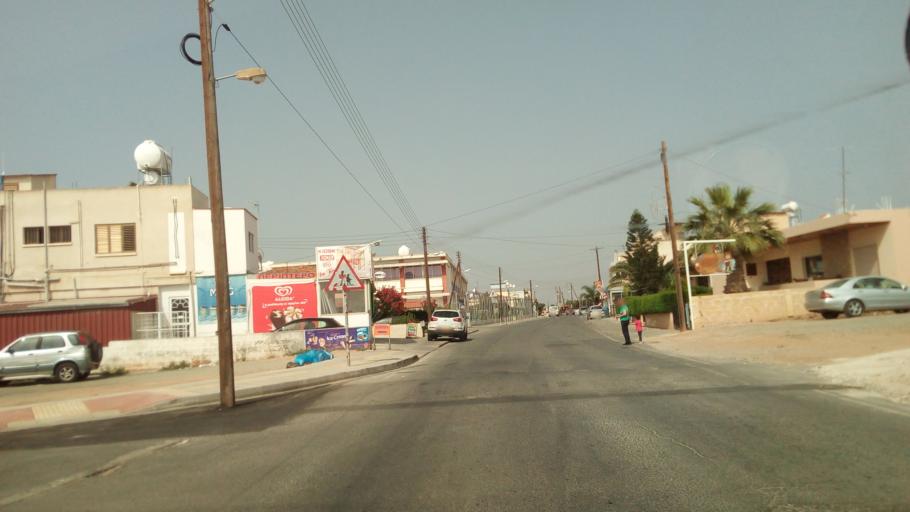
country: CY
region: Limassol
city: Ypsonas
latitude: 34.6868
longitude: 32.9657
